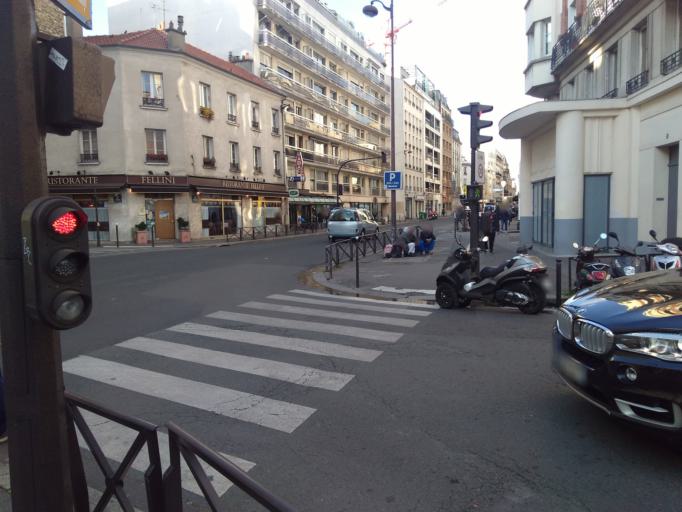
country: FR
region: Ile-de-France
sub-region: Departement des Hauts-de-Seine
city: Vanves
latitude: 48.8451
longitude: 2.2976
